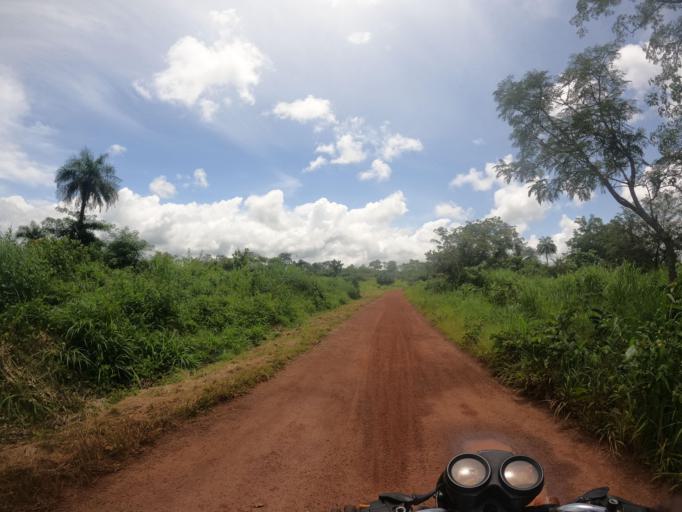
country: SL
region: Northern Province
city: Makeni
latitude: 9.1301
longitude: -12.2441
